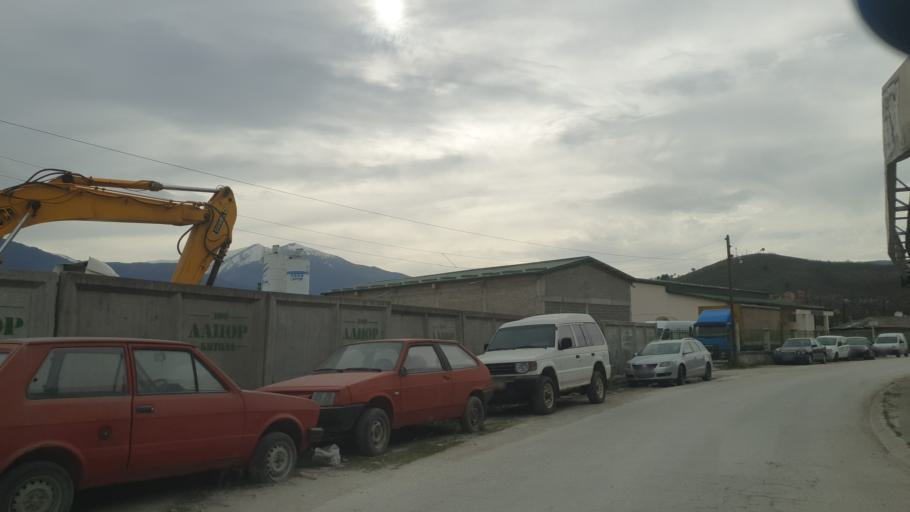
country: MK
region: Bitola
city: Gorno Orizari
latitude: 41.0367
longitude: 21.3511
